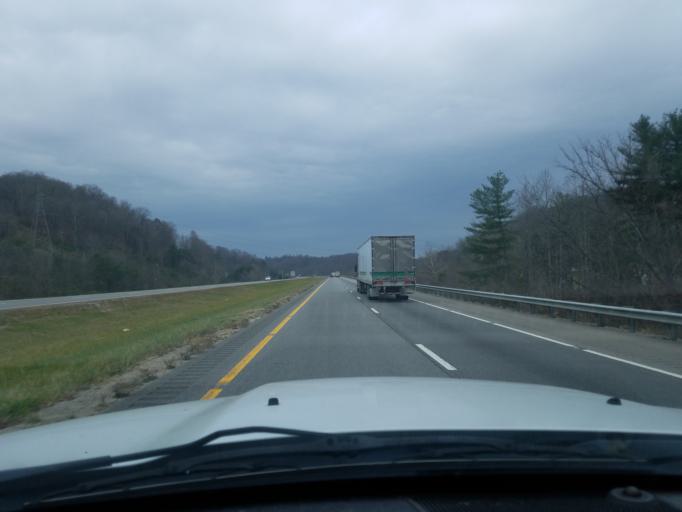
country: US
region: Kentucky
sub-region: Boyd County
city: Catlettsburg
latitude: 38.3818
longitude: -82.6312
